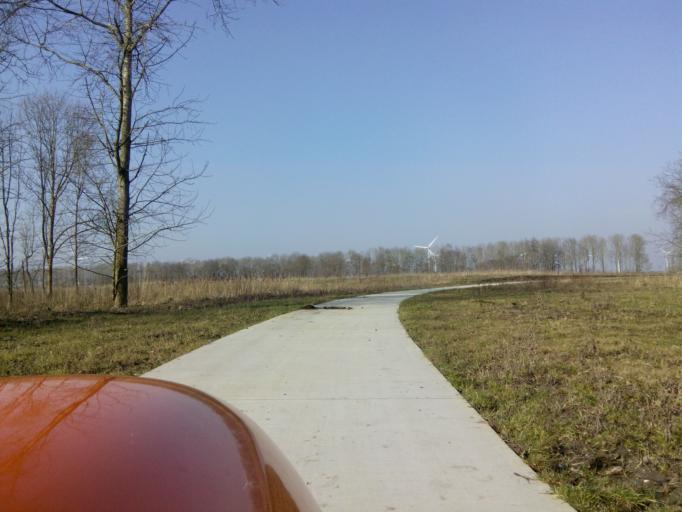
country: NL
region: Flevoland
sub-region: Gemeente Zeewolde
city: Zeewolde
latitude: 52.3219
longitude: 5.4494
